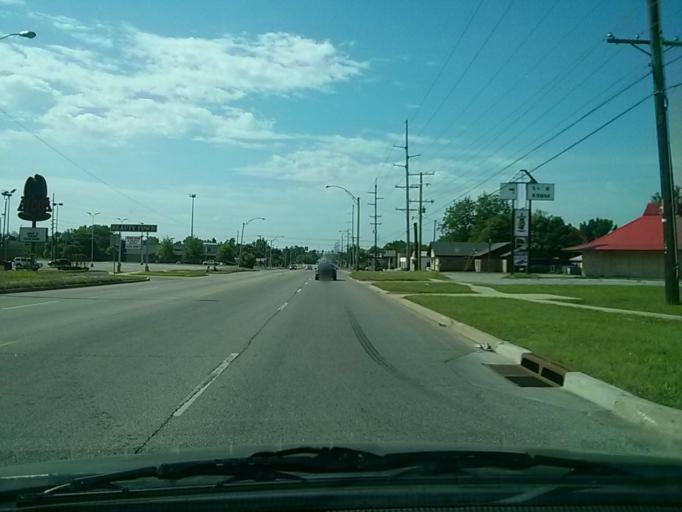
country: US
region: Oklahoma
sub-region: Tulsa County
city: Turley
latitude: 36.2226
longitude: -95.9757
